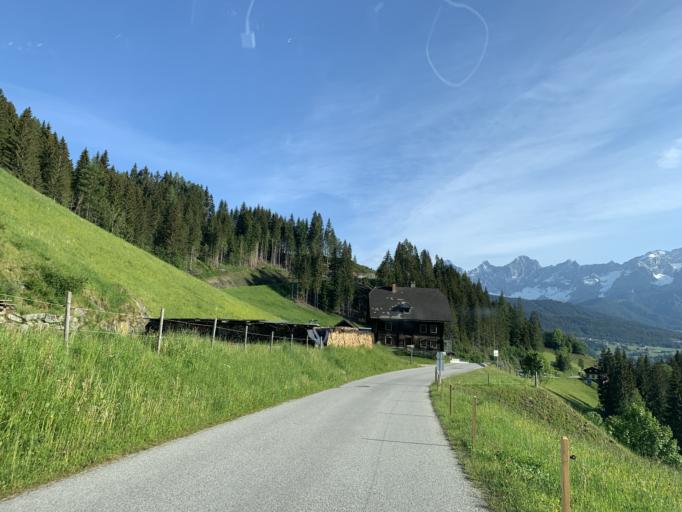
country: AT
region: Styria
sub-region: Politischer Bezirk Liezen
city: Schladming
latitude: 47.3733
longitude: 13.6142
